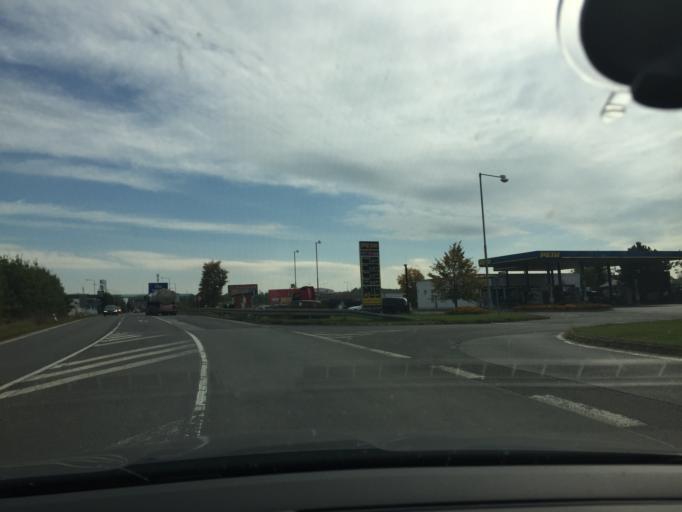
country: CZ
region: Praha
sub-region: Praha 14
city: Dolni Pocernice
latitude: 50.0827
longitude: 14.5855
